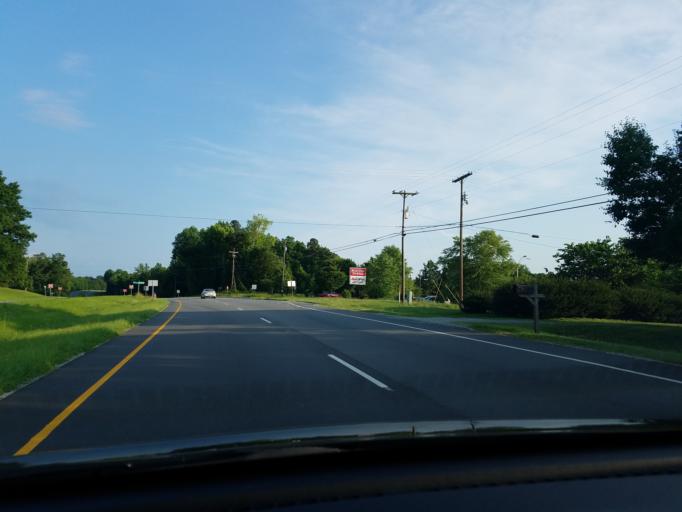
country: US
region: North Carolina
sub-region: Durham County
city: Gorman
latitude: 36.1344
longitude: -78.9052
